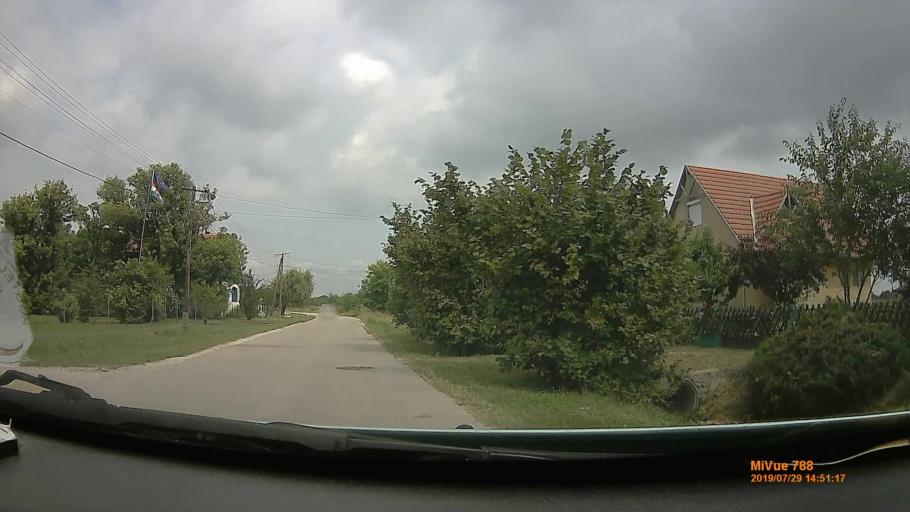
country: HU
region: Fejer
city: Lepseny
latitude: 47.0149
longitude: 18.2087
